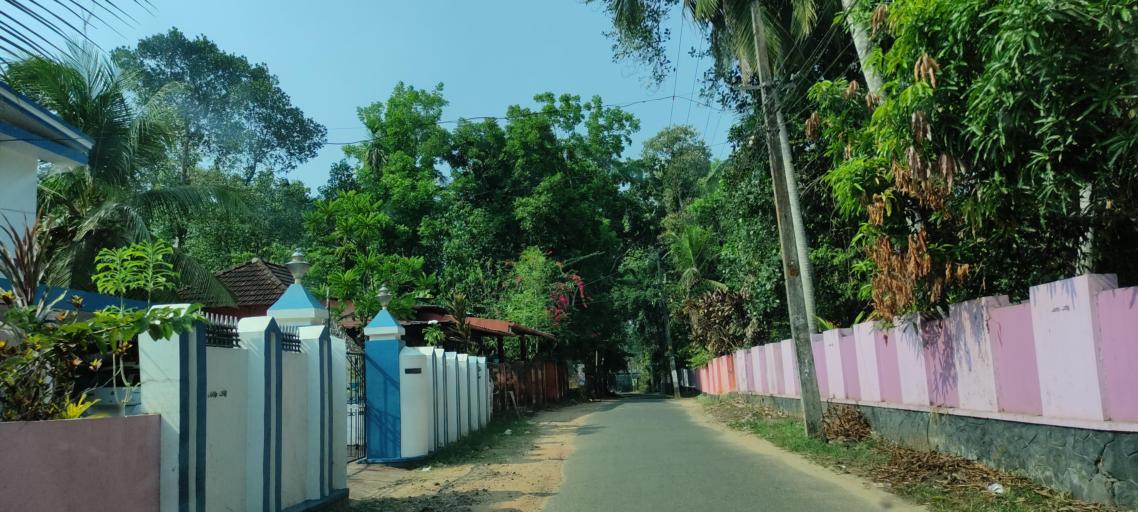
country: IN
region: Kerala
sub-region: Pattanamtitta
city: Tiruvalla
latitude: 9.3491
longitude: 76.5276
